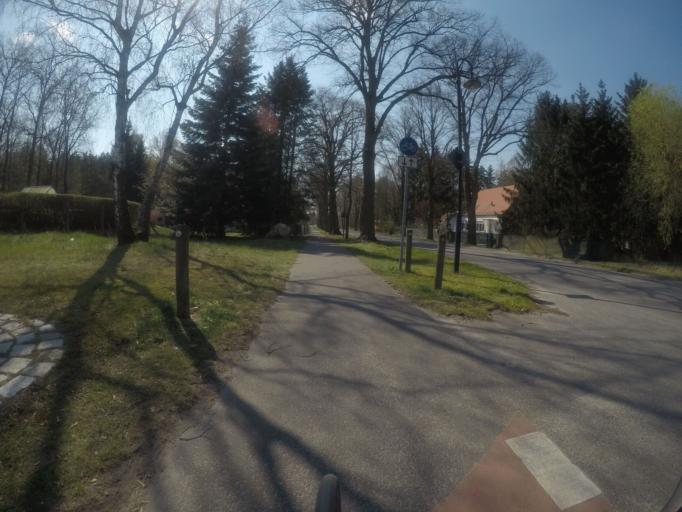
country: DE
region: Brandenburg
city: Brieselang
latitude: 52.6500
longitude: 13.0060
